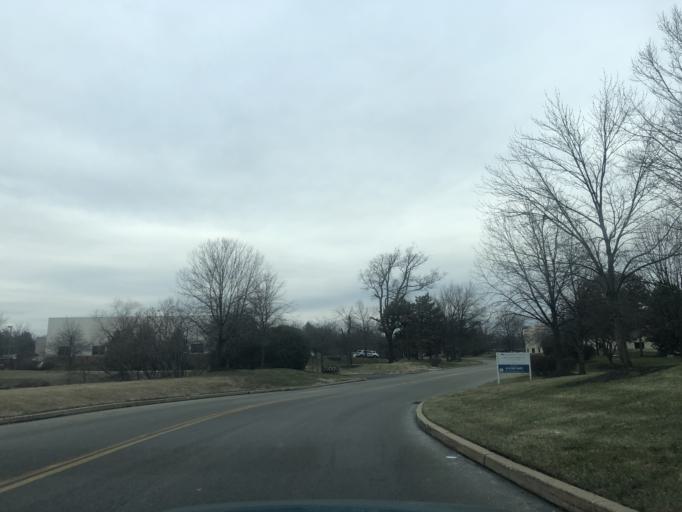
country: US
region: Pennsylvania
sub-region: Montgomery County
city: Bridgeport
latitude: 40.0862
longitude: -75.3398
